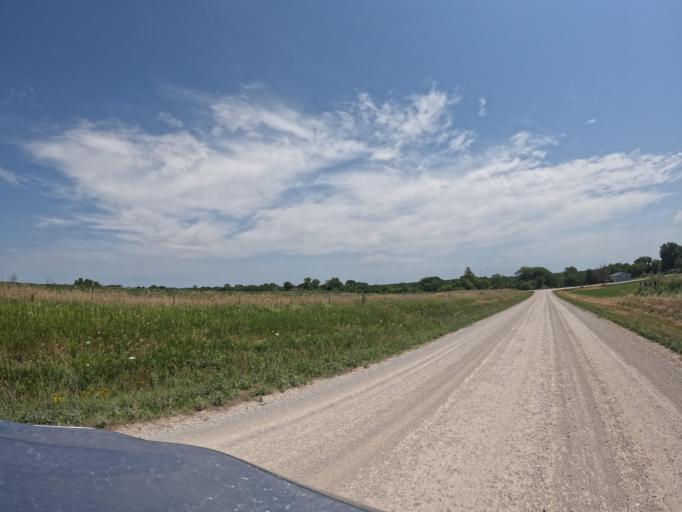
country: US
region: Iowa
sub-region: Appanoose County
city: Centerville
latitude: 40.7874
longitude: -92.9081
